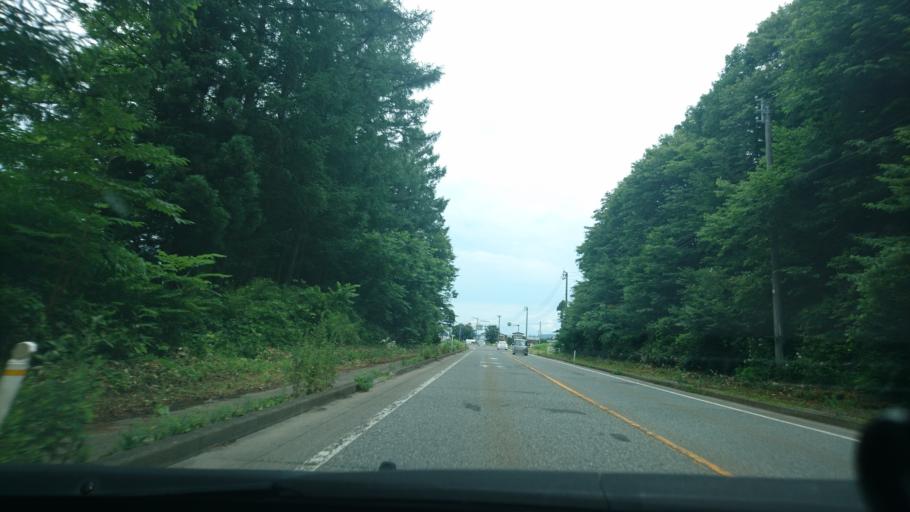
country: JP
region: Akita
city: Yokotemachi
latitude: 39.3885
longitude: 140.5680
